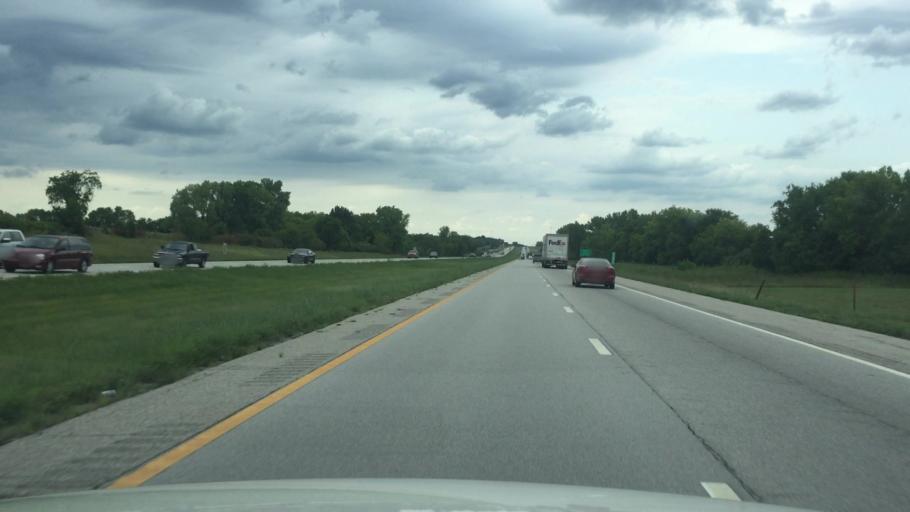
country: US
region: Kansas
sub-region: Miami County
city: Louisburg
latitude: 38.7559
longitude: -94.6774
